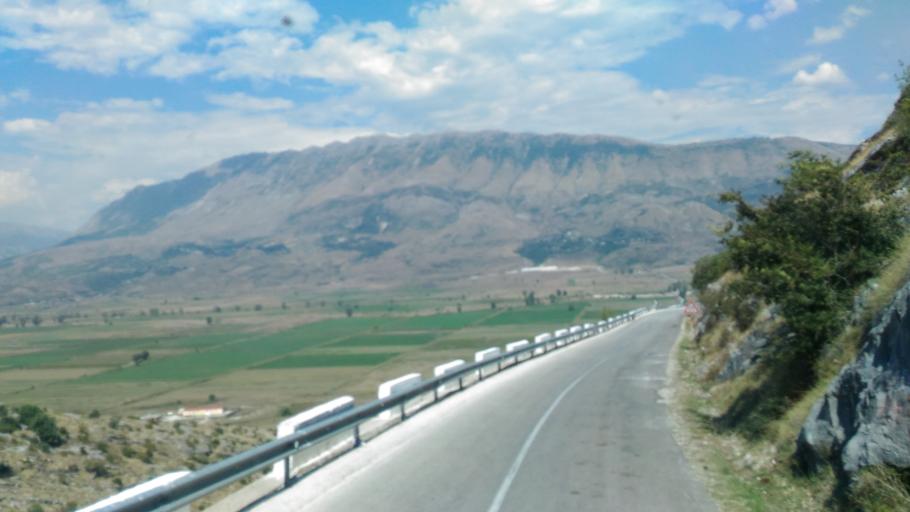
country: AL
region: Gjirokaster
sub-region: Rrethi i Gjirokastres
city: Libohove
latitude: 39.9464
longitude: 20.2526
